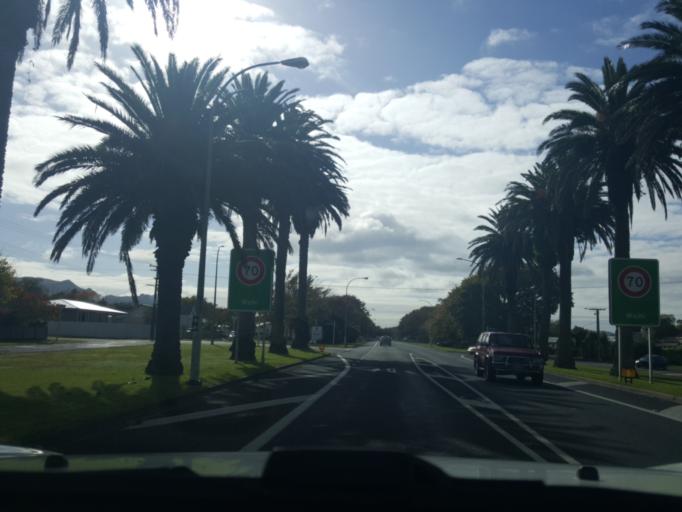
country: NZ
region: Waikato
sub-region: Hauraki District
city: Waihi
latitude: -37.3965
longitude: 175.8282
